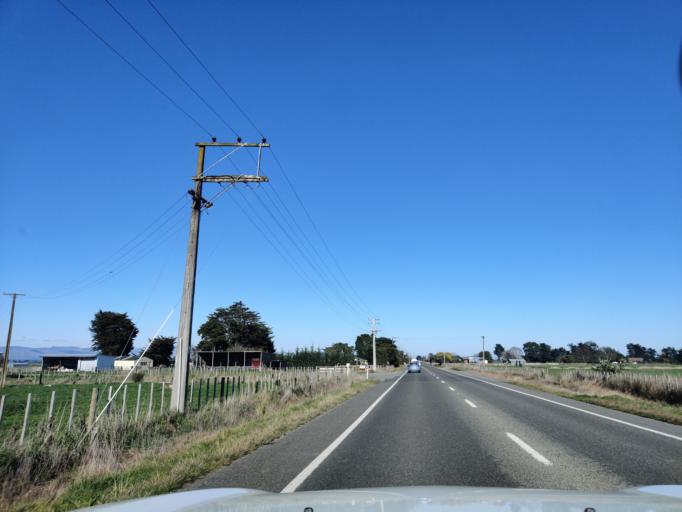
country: NZ
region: Manawatu-Wanganui
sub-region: Palmerston North City
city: Palmerston North
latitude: -40.2562
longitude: 175.5754
